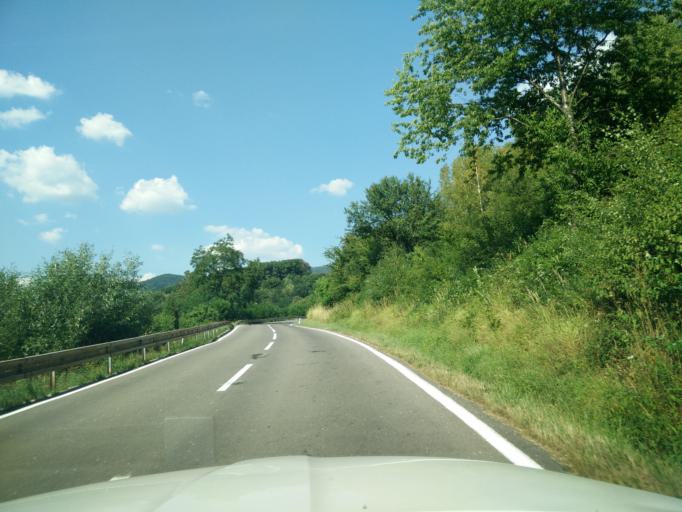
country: SK
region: Nitriansky
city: Bojnice
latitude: 48.8083
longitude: 18.5047
